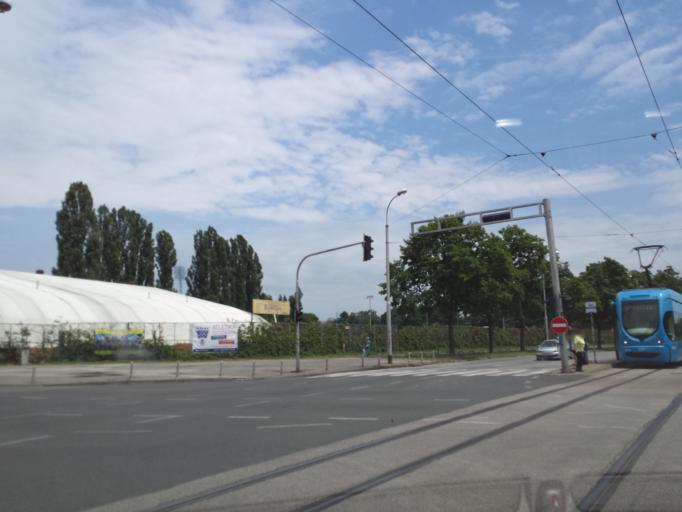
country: HR
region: Grad Zagreb
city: Zagreb
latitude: 45.8153
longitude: 16.0131
